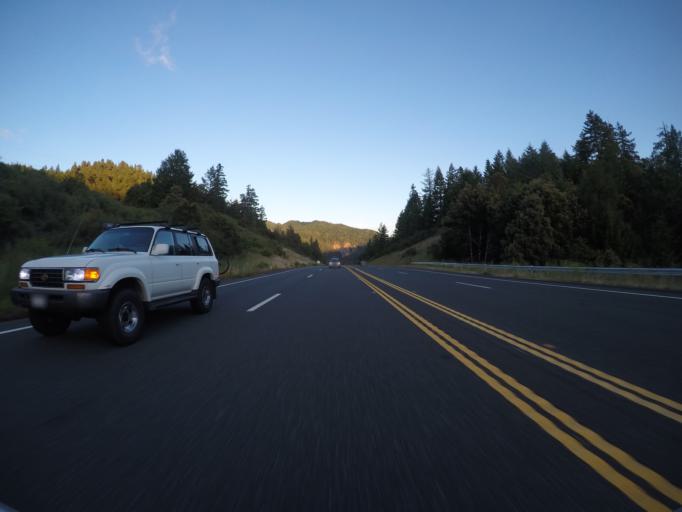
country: US
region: California
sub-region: Humboldt County
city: Redway
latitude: 39.9390
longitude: -123.7761
